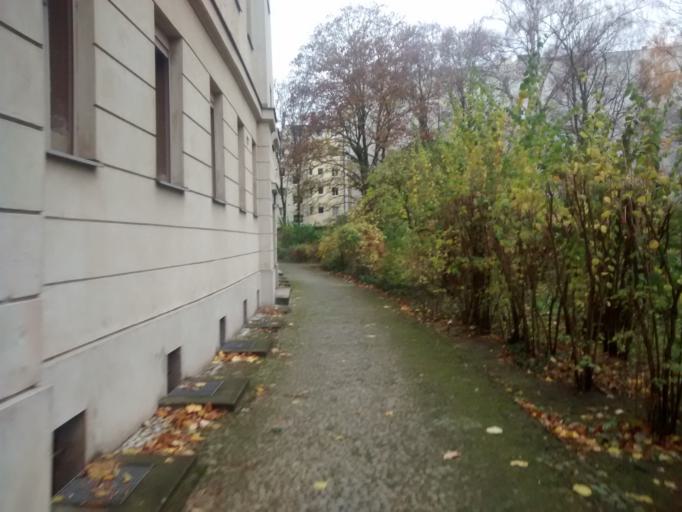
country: DE
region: Berlin
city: Moabit
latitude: 52.5245
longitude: 13.3414
